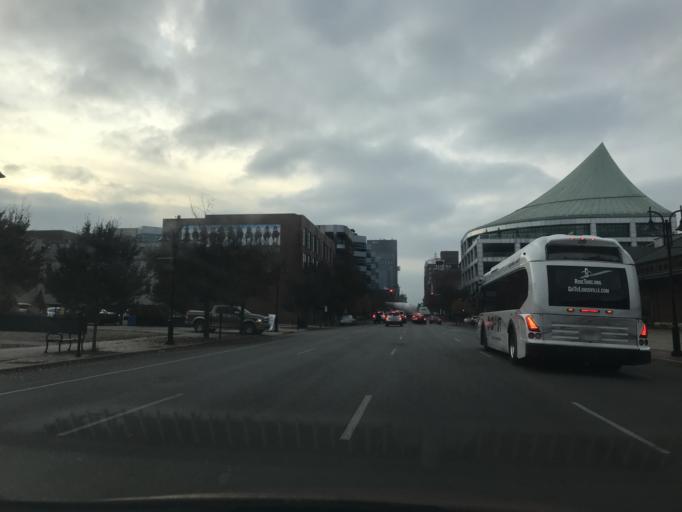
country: US
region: Kentucky
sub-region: Jefferson County
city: Louisville
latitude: 38.2553
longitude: -85.7446
